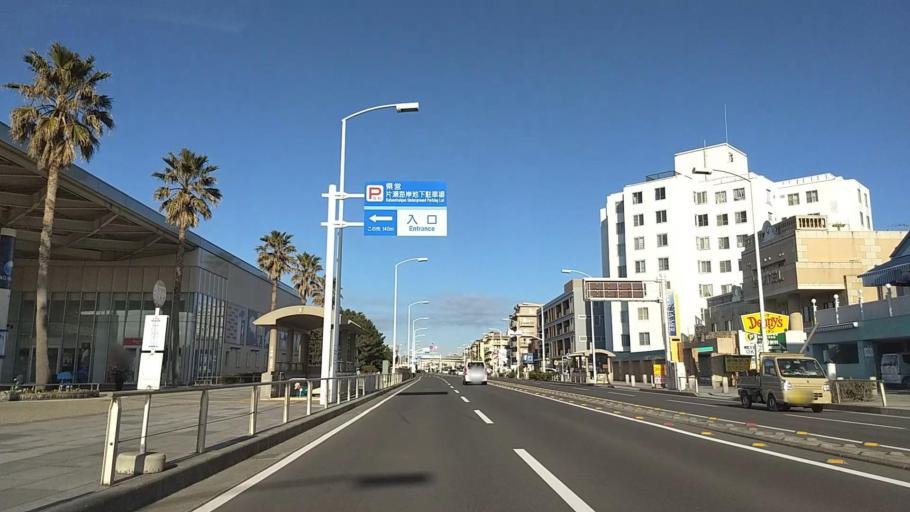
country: JP
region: Kanagawa
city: Fujisawa
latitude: 35.3093
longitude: 139.4807
